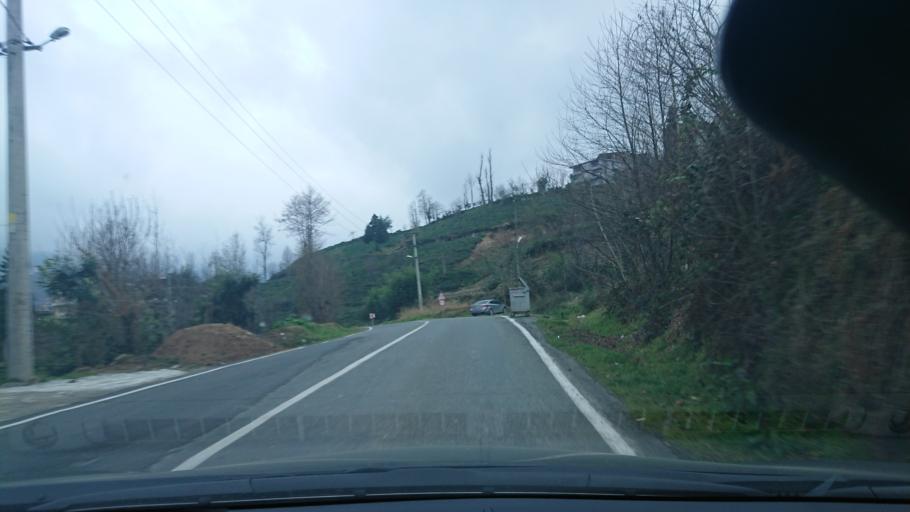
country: TR
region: Rize
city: Rize
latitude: 41.0027
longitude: 40.4867
